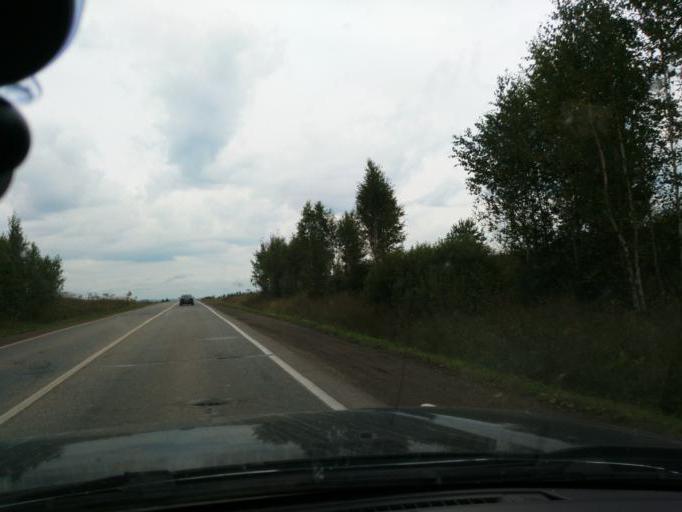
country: RU
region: Perm
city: Chernushka
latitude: 56.7119
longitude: 56.1817
